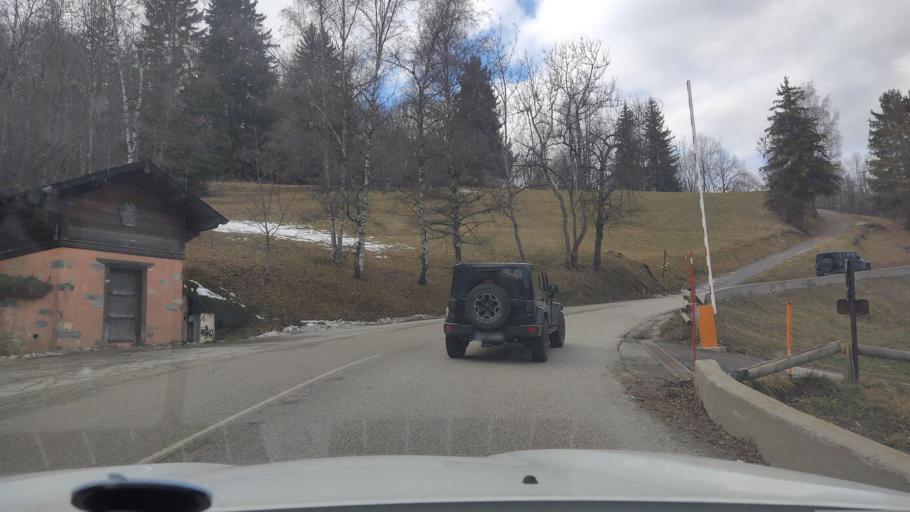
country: FR
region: Rhone-Alpes
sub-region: Departement de la Savoie
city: Saint-Bon-Tarentaise
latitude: 45.4323
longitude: 6.6339
